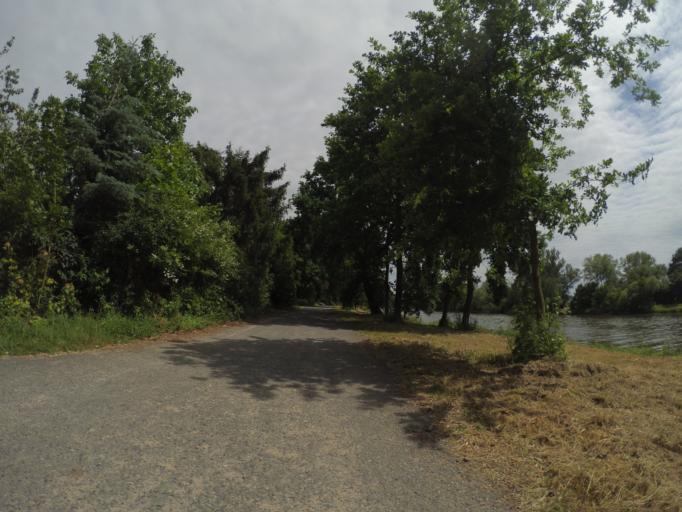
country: CZ
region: Central Bohemia
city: Lysa nad Labem
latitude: 50.1725
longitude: 14.8760
